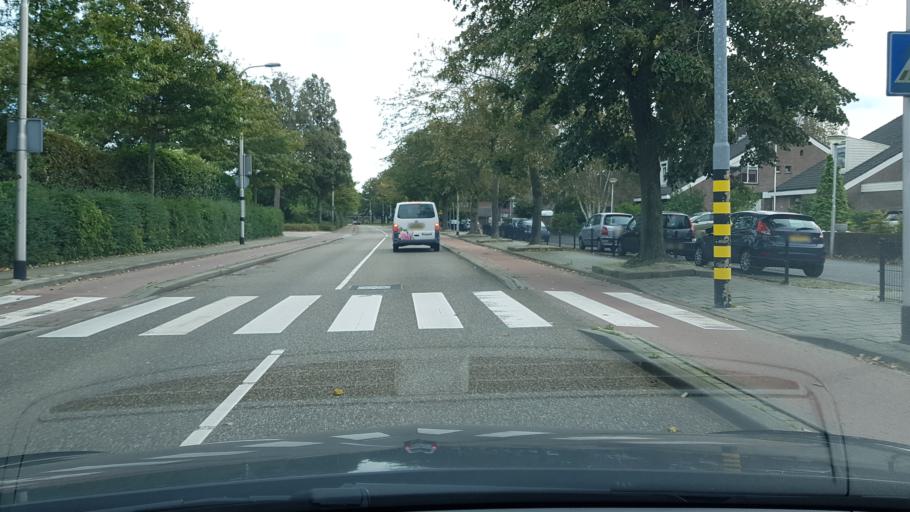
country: NL
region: South Holland
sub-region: Gemeente Hillegom
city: Hillegom
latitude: 52.2864
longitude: 4.5815
